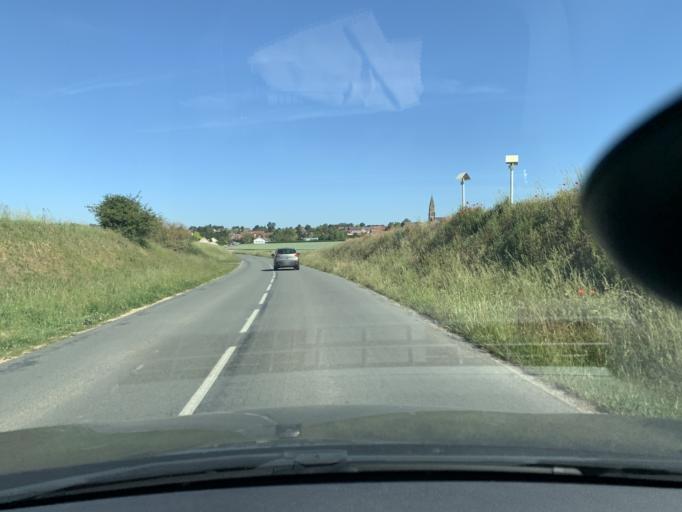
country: FR
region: Nord-Pas-de-Calais
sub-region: Departement du Nord
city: Fontaine-Notre-Dame
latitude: 50.1589
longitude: 3.1605
